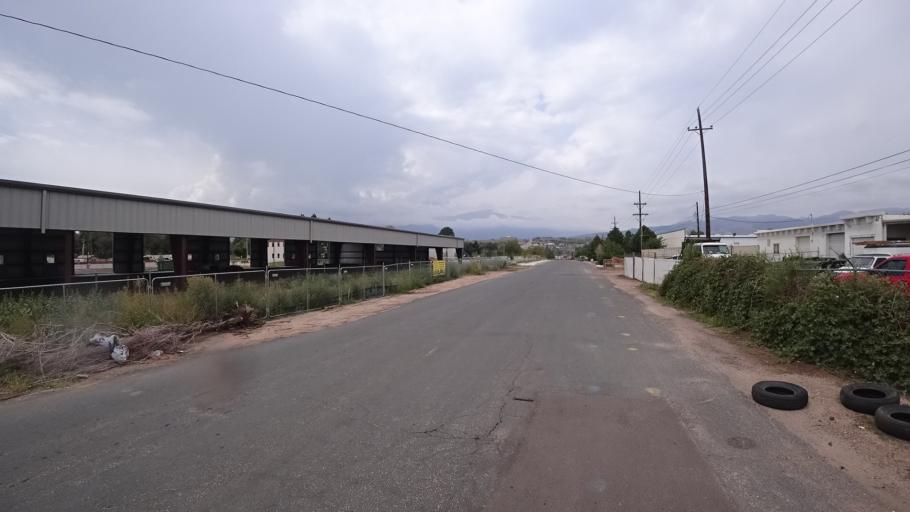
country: US
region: Colorado
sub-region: El Paso County
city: Colorado Springs
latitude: 38.8777
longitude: -104.8230
